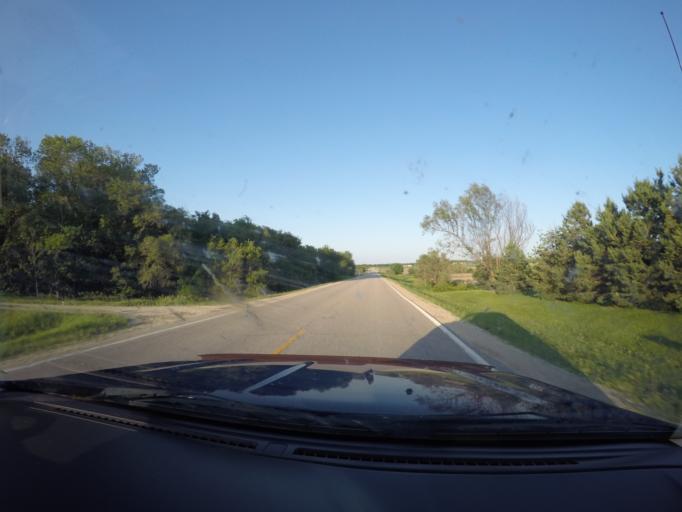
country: US
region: Kansas
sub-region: Marshall County
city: Blue Rapids
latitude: 39.6897
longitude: -96.7720
